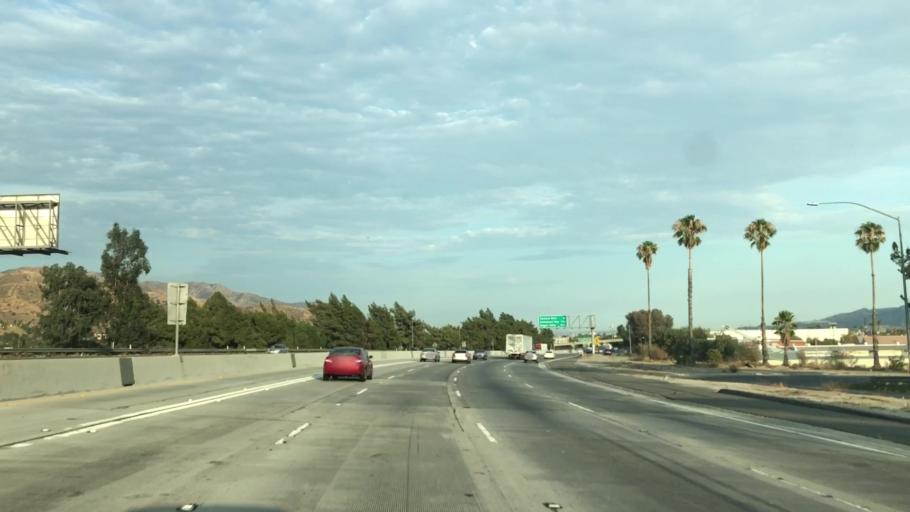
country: US
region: California
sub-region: Los Angeles County
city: North Hollywood
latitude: 34.2261
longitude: -118.3756
